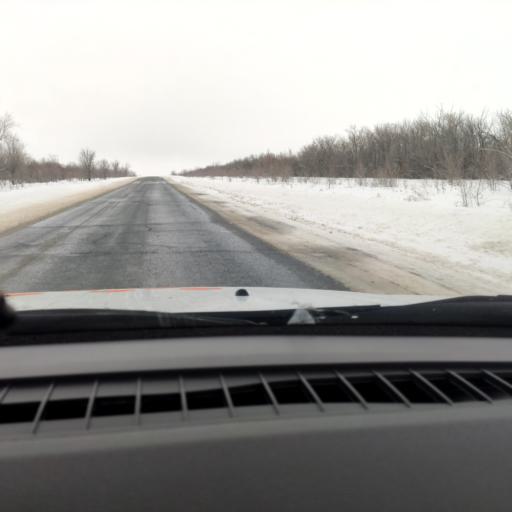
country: RU
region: Samara
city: Mayskoye
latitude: 52.4427
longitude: 50.5356
